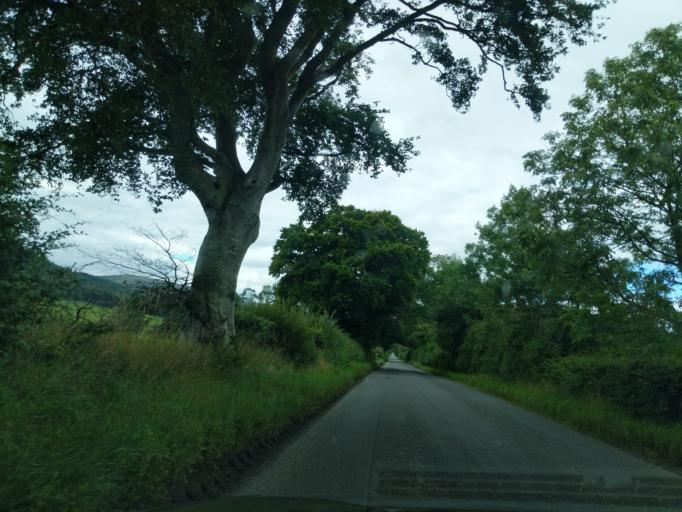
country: GB
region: Scotland
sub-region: The Scottish Borders
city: Peebles
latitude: 55.6288
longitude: -3.2933
